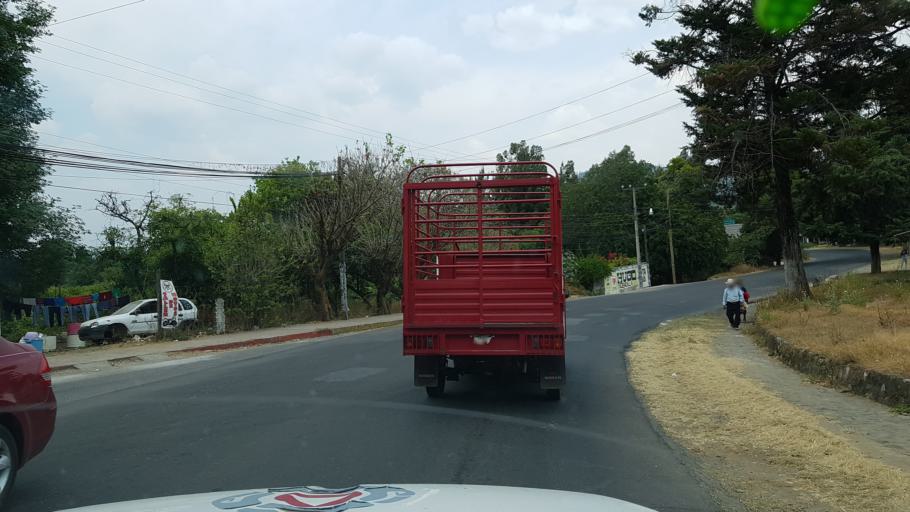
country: MX
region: Morelos
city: Ocuituco
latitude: 18.8785
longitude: -98.7821
